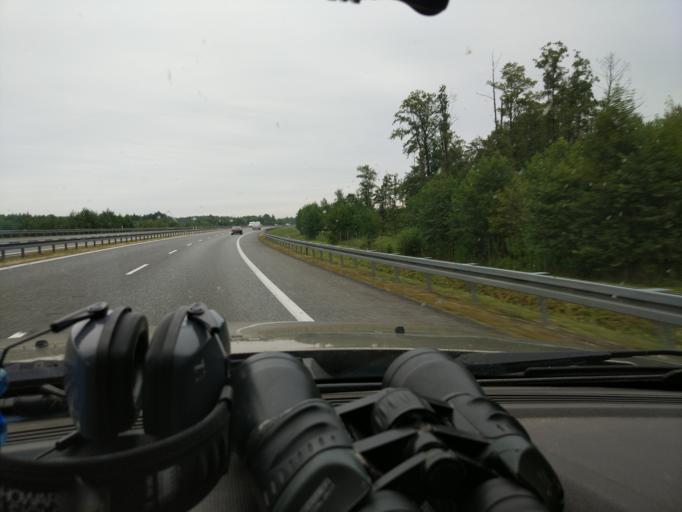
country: PL
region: Masovian Voivodeship
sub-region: Powiat wyszkowski
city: Wyszkow
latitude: 52.5698
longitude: 21.4713
